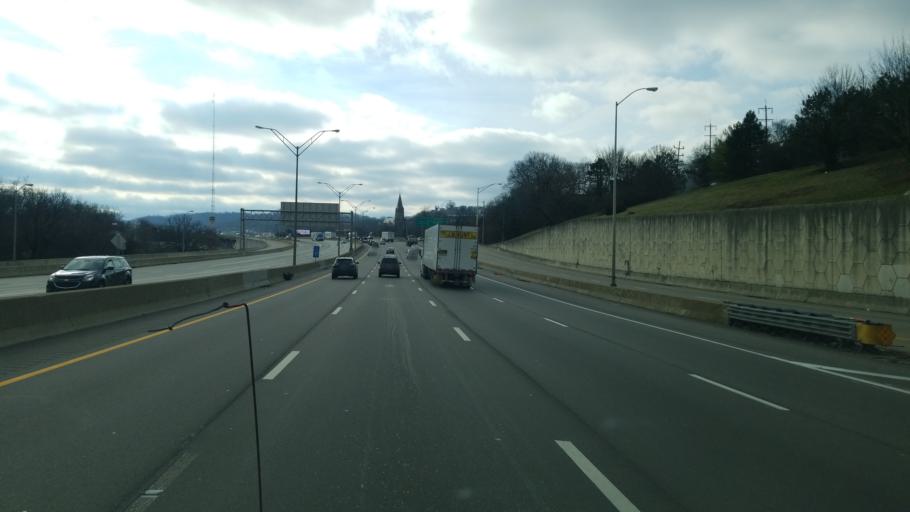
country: US
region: Kentucky
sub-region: Kenton County
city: Covington
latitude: 39.0825
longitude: -84.5229
